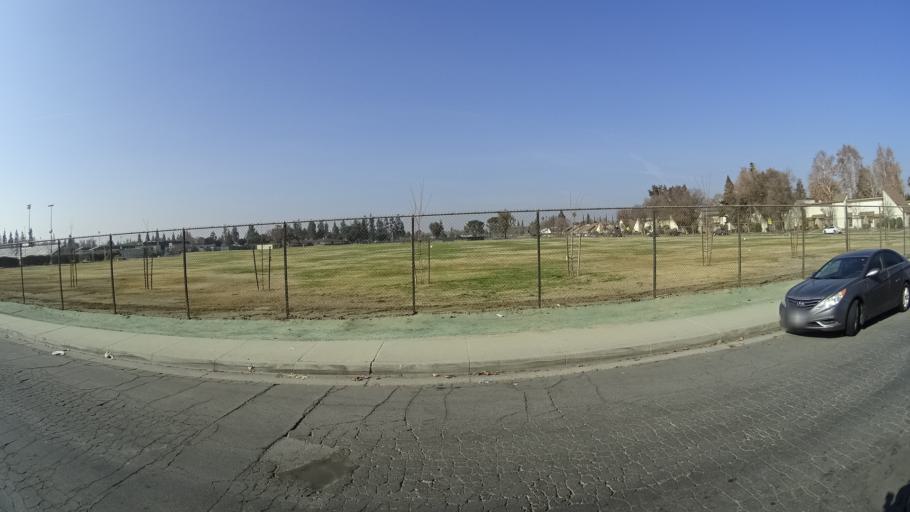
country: US
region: California
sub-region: Kern County
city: Bakersfield
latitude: 35.3447
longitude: -119.0549
